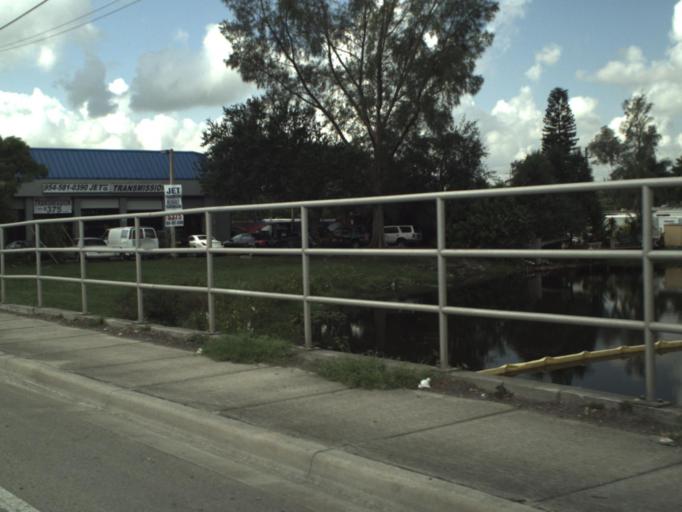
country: US
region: Florida
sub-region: Broward County
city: Davie
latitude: 26.0659
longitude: -80.2081
